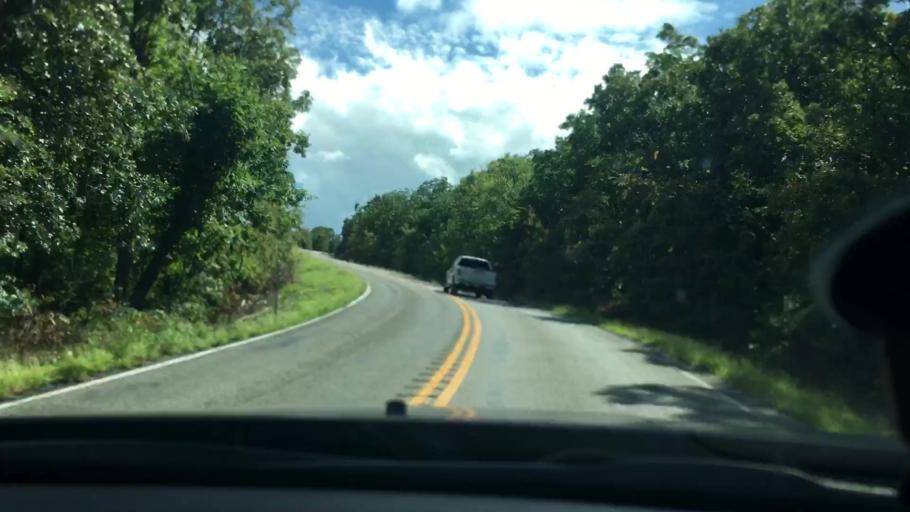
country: US
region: Oklahoma
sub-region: Sequoyah County
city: Vian
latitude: 35.6329
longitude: -94.9638
